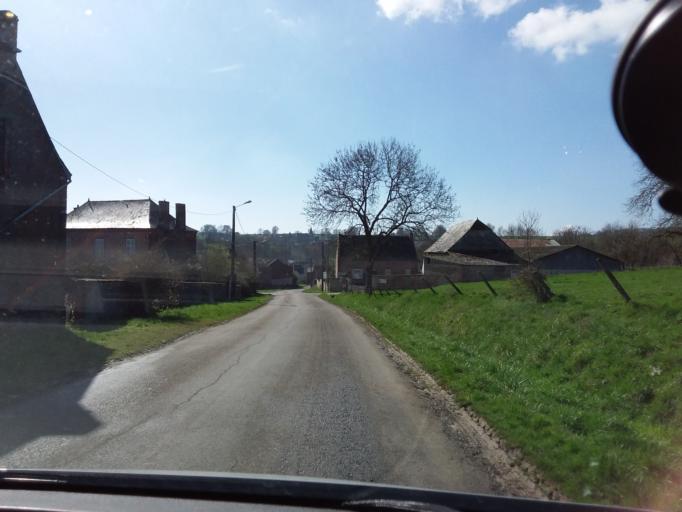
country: FR
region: Picardie
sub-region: Departement de l'Aisne
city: Montcornet
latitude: 49.7859
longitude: 4.0050
